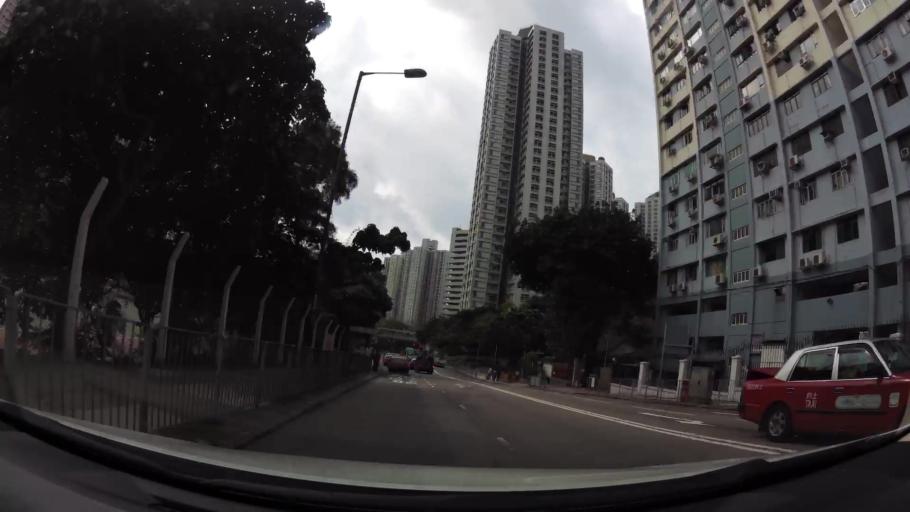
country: HK
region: Kowloon City
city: Kowloon
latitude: 22.3210
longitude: 114.2267
